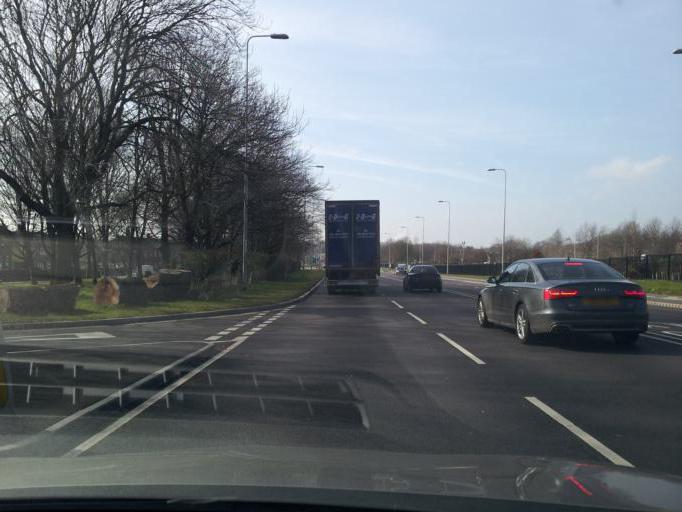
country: GB
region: England
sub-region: Nottinghamshire
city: Ruddington
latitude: 52.9103
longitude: -1.1830
